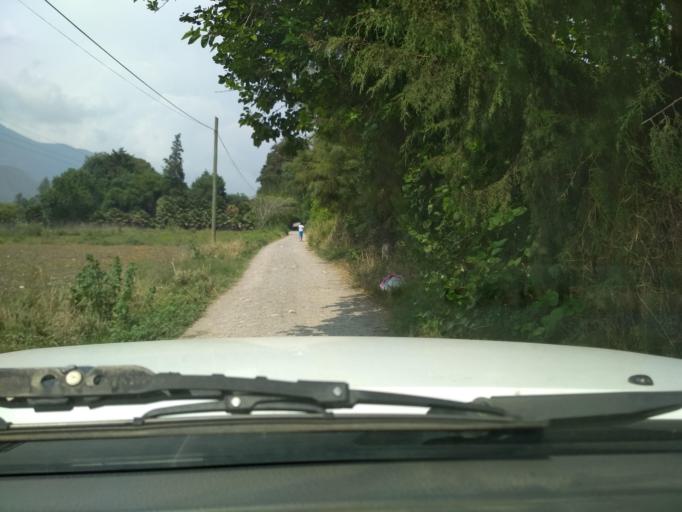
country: MX
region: Veracruz
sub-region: Acultzingo
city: Acatla
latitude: 18.7637
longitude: -97.2214
